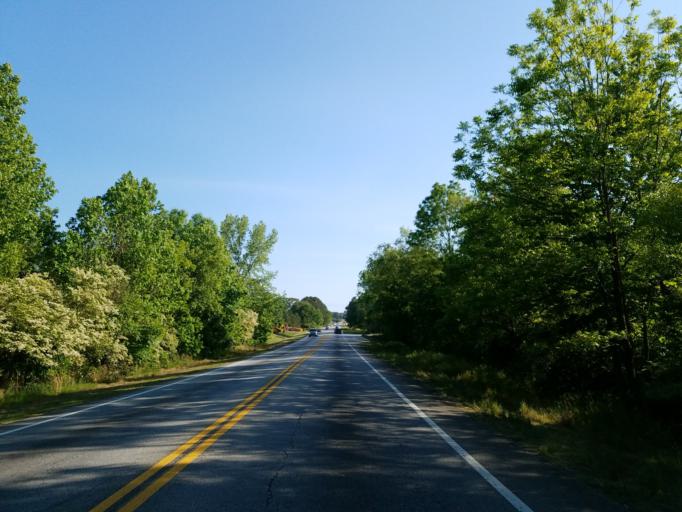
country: US
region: Georgia
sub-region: Carroll County
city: Villa Rica
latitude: 33.7373
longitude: -84.9377
